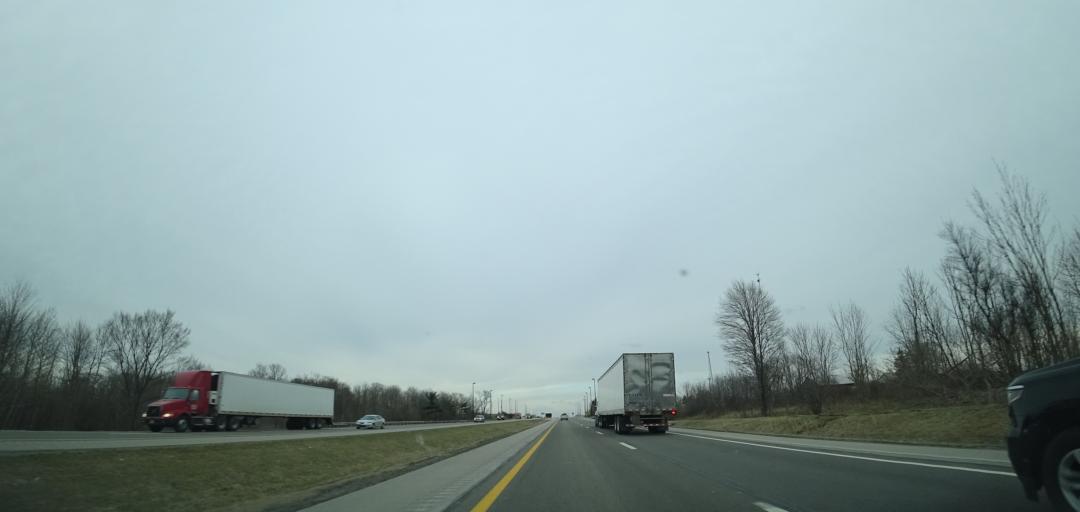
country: US
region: Ohio
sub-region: Mahoning County
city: New Middletown
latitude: 40.9408
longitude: -80.5943
